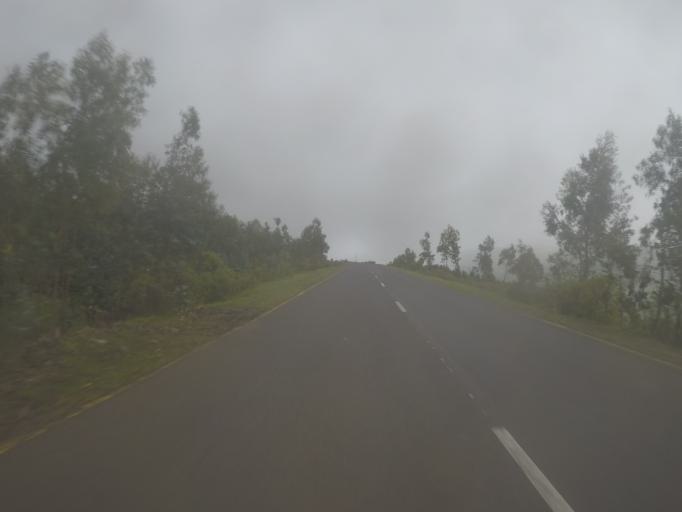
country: ET
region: Amhara
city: Gondar
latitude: 12.7450
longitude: 37.5254
